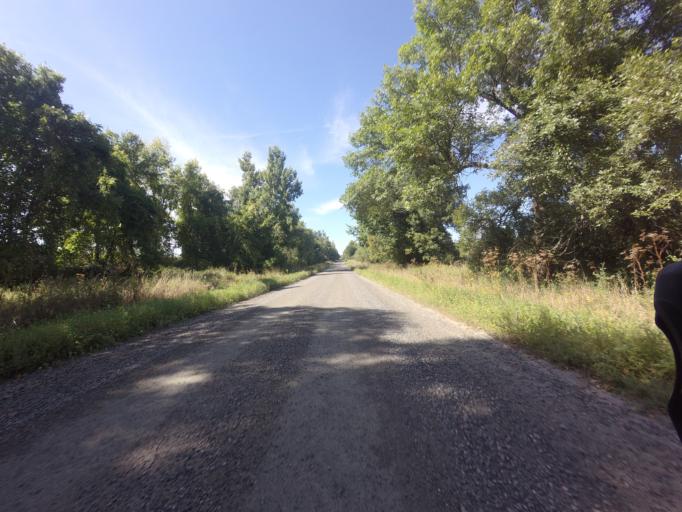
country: CA
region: Ontario
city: Perth
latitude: 44.9565
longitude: -76.3333
